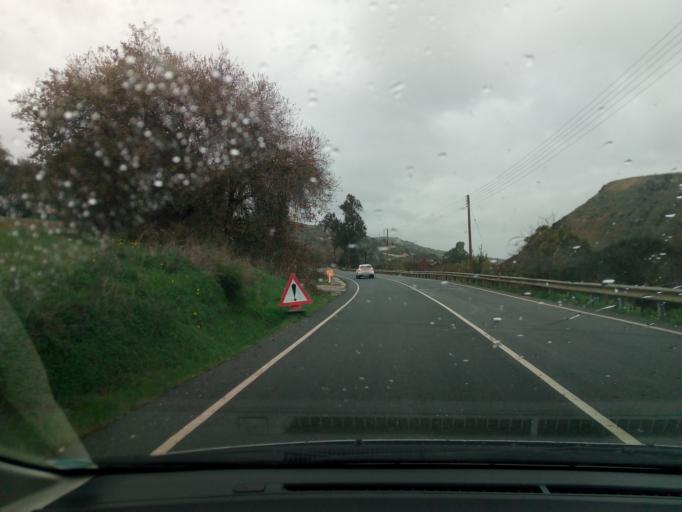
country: CY
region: Pafos
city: Polis
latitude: 34.9591
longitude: 32.4616
